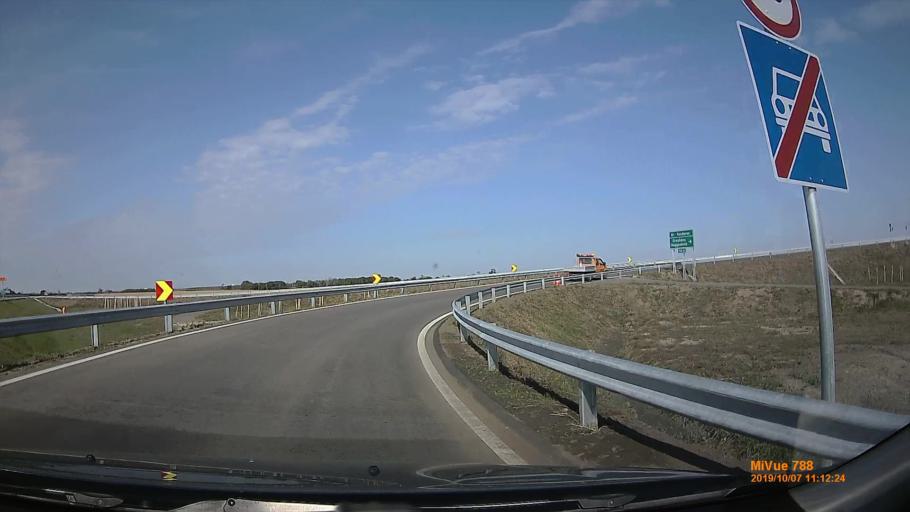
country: HU
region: Bekes
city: Kondoros
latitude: 46.7397
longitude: 20.7823
